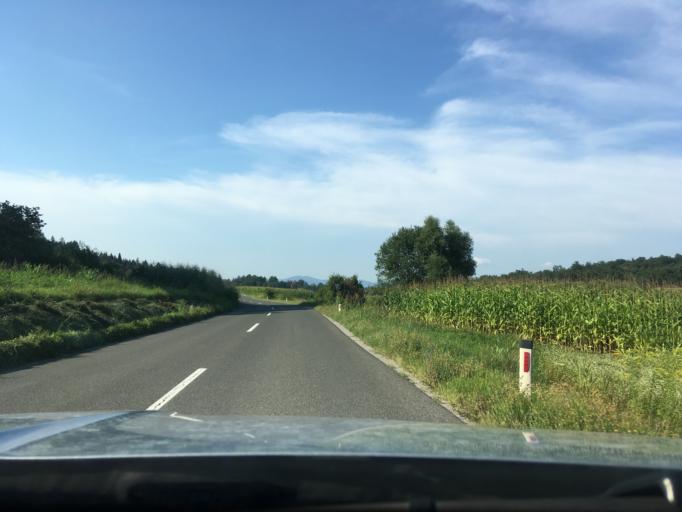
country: SI
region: Crnomelj
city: Crnomelj
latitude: 45.4985
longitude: 15.1915
